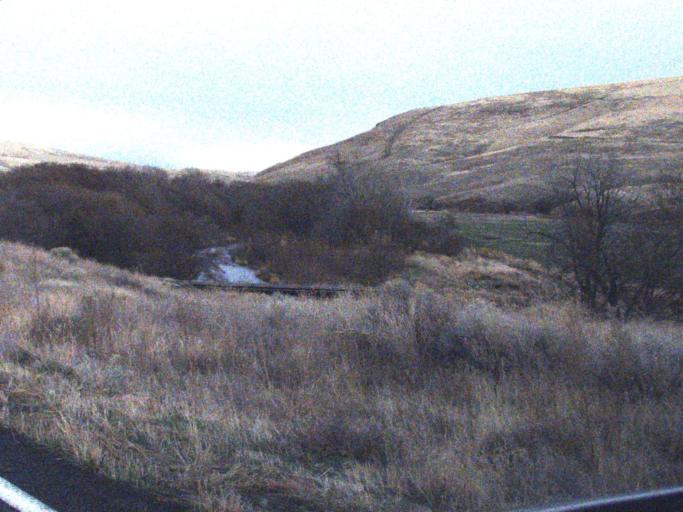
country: US
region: Washington
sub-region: Columbia County
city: Dayton
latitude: 46.5088
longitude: -117.9974
